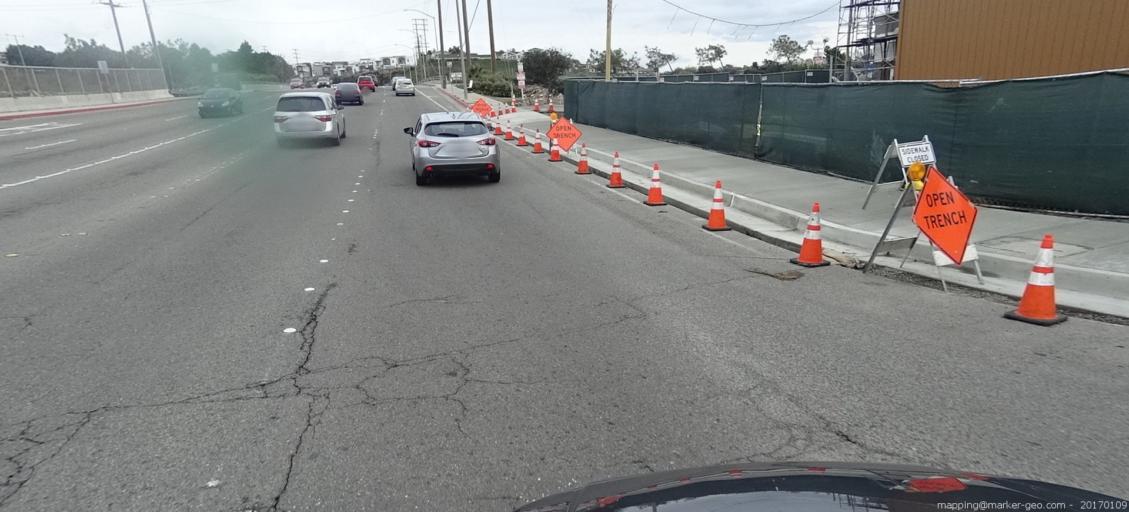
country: US
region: California
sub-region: Orange County
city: Costa Mesa
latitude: 33.6505
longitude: -117.9534
